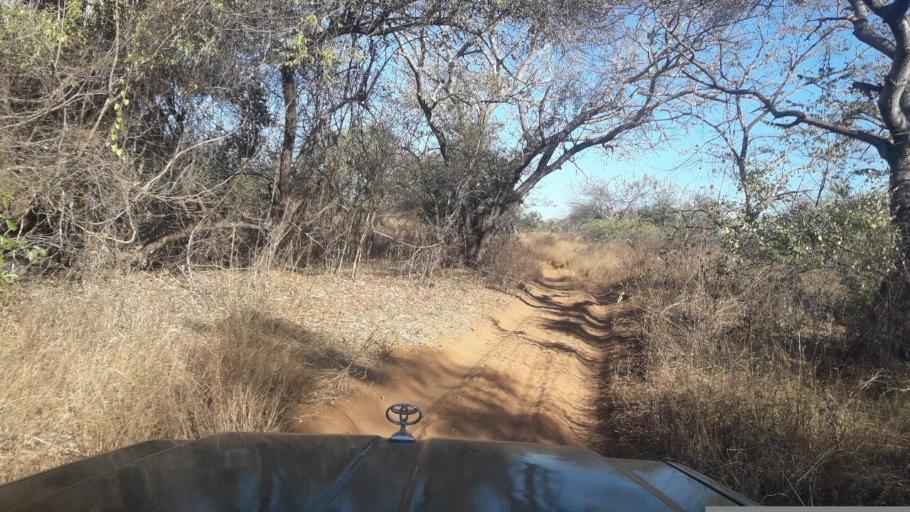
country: MG
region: Boeny
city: Sitampiky
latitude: -16.4112
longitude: 45.6027
